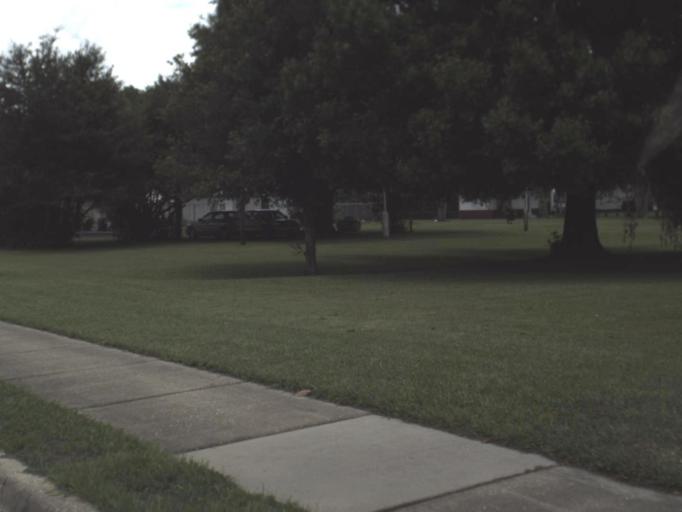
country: US
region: Florida
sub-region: Hillsborough County
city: Plant City
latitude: 28.0185
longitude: -82.1072
